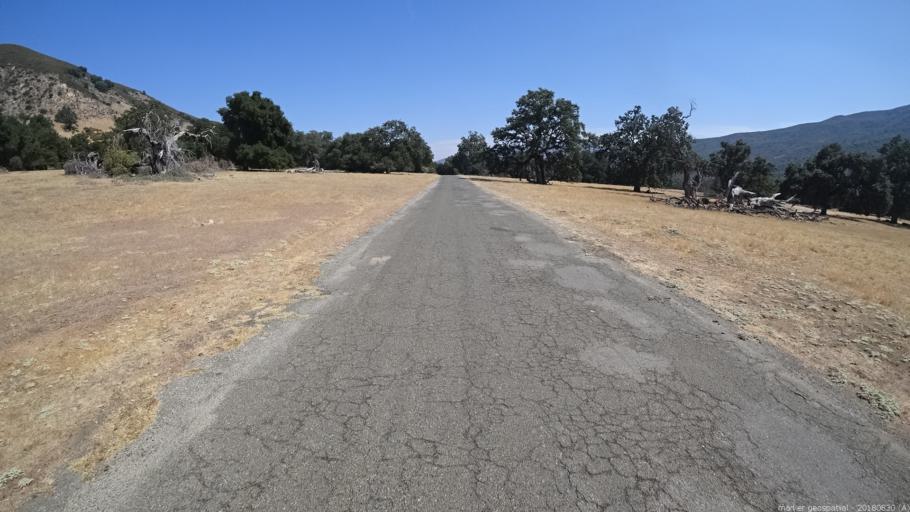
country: US
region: California
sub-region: Monterey County
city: Greenfield
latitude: 36.0946
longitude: -121.4222
